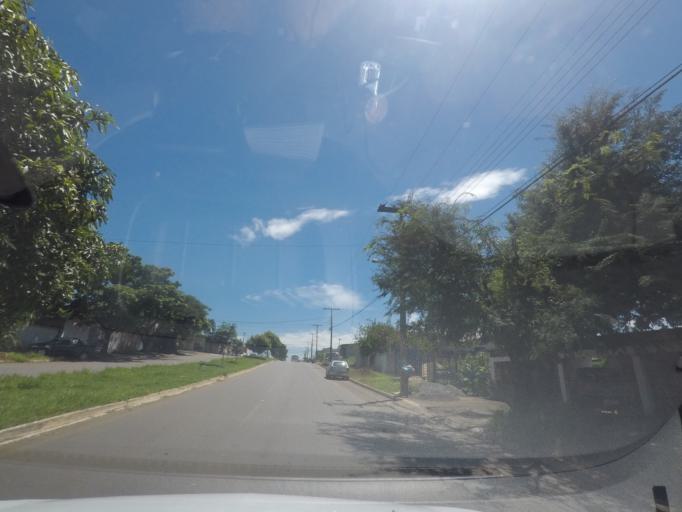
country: BR
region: Goias
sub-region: Aparecida De Goiania
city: Aparecida de Goiania
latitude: -16.7725
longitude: -49.3247
